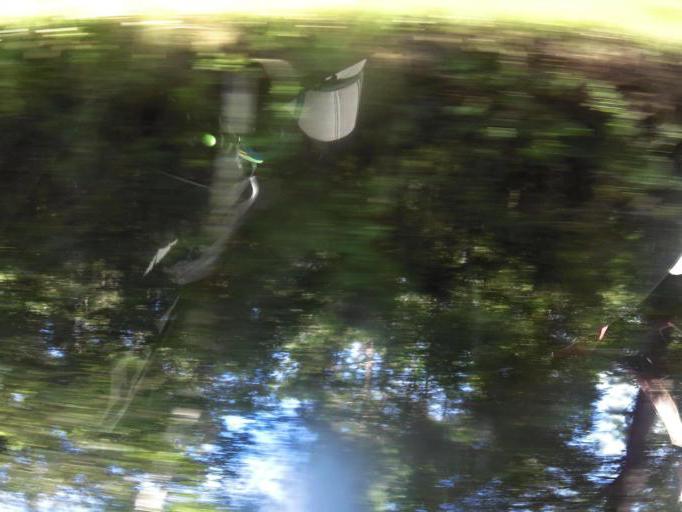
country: US
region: Florida
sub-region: Clay County
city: Green Cove Springs
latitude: 29.9202
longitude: -81.5496
